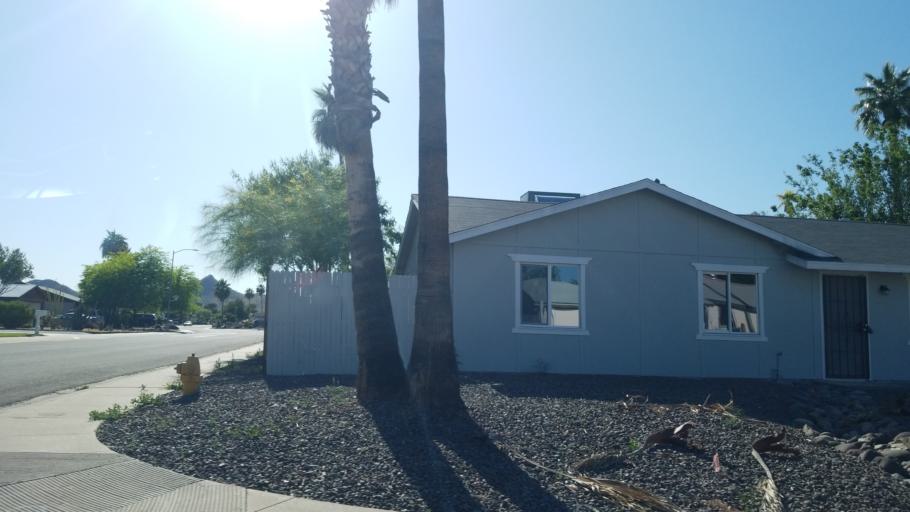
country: US
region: Arizona
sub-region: Maricopa County
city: Paradise Valley
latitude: 33.6172
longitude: -112.0003
